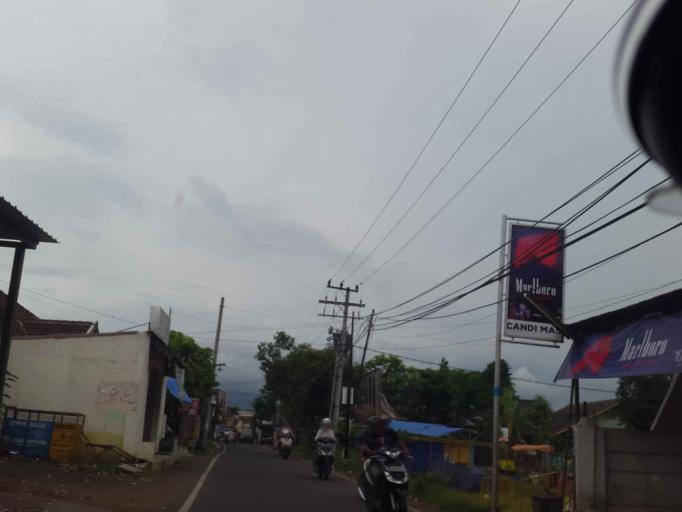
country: ID
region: East Java
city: Malang
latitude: -7.9583
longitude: 112.5993
